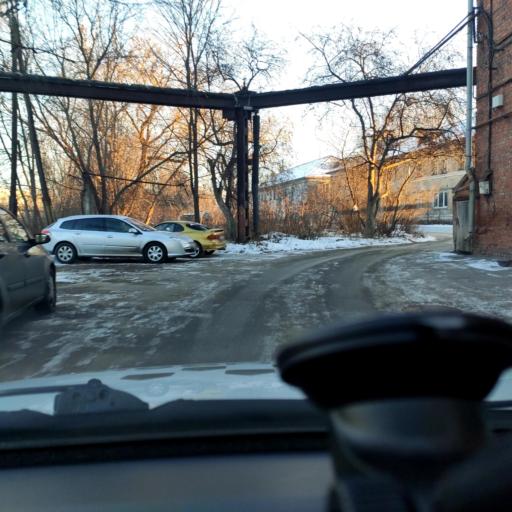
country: RU
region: Perm
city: Perm
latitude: 58.0391
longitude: 56.3088
